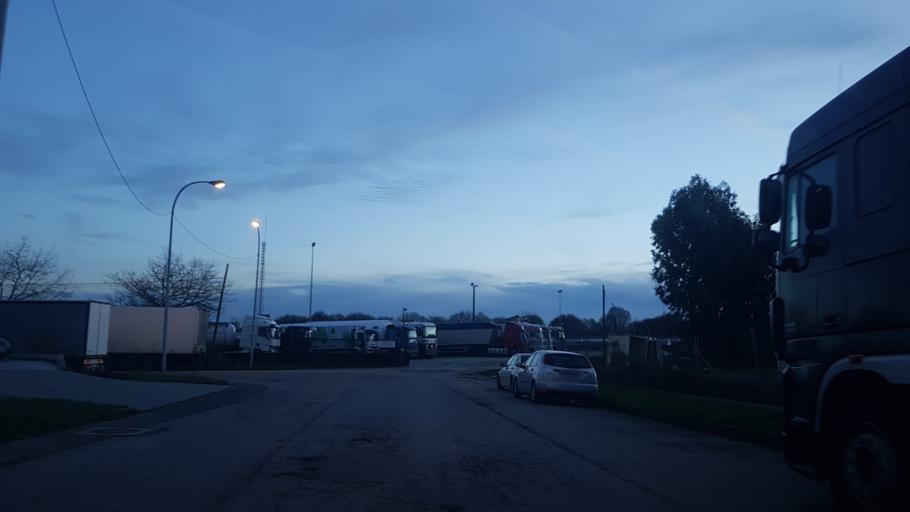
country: ES
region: Galicia
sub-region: Provincia de Lugo
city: Lugo
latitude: 43.0458
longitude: -7.5729
